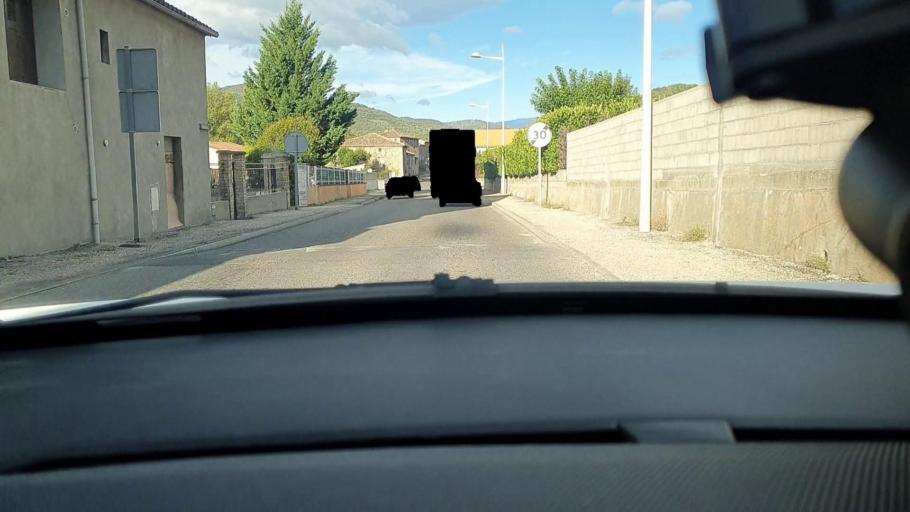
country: FR
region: Languedoc-Roussillon
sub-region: Departement du Gard
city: Molieres-sur-Ceze
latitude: 44.2767
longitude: 4.1476
